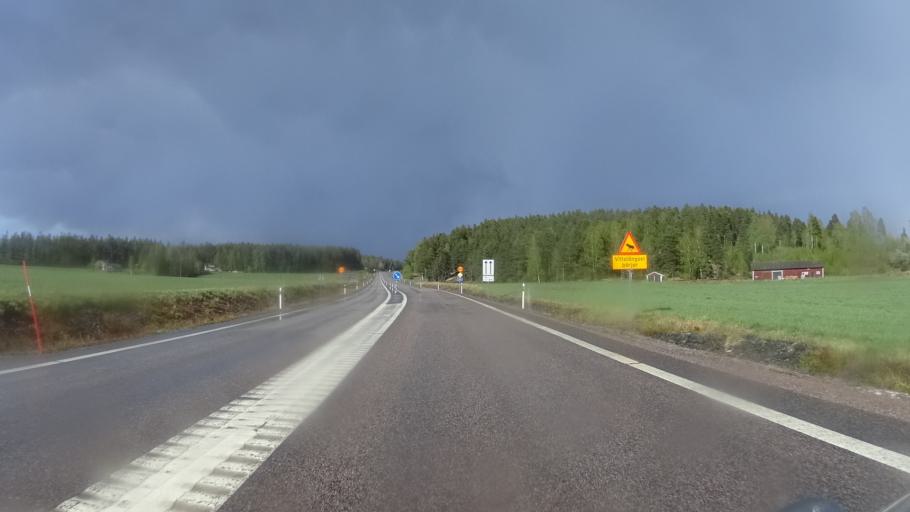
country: SE
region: OErebro
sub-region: Askersunds Kommun
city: Askersund
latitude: 58.7864
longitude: 14.8126
